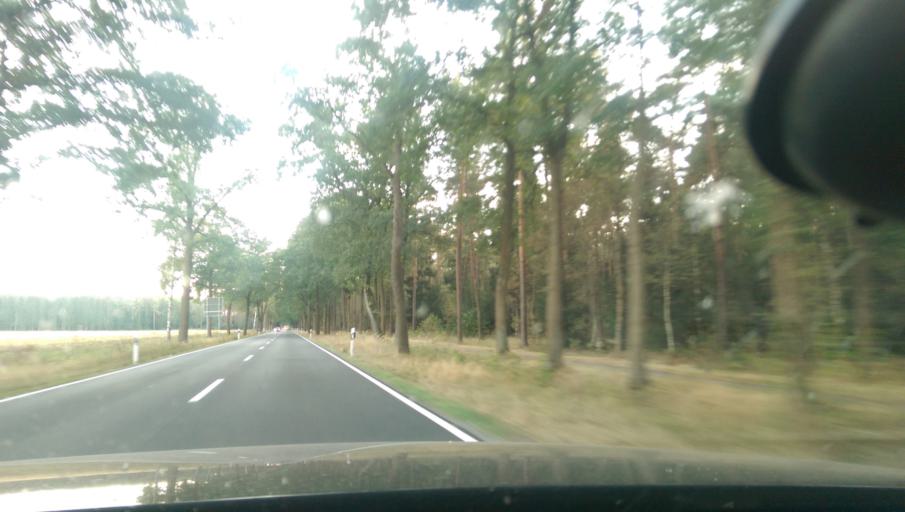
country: DE
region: Lower Saxony
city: Hodenhagen
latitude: 52.7957
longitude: 9.5898
